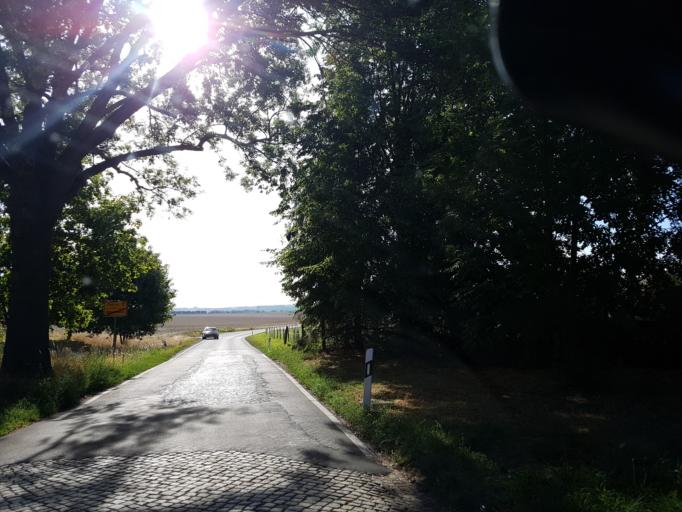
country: DE
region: Saxony
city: Naundorf
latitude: 51.2283
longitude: 13.1324
